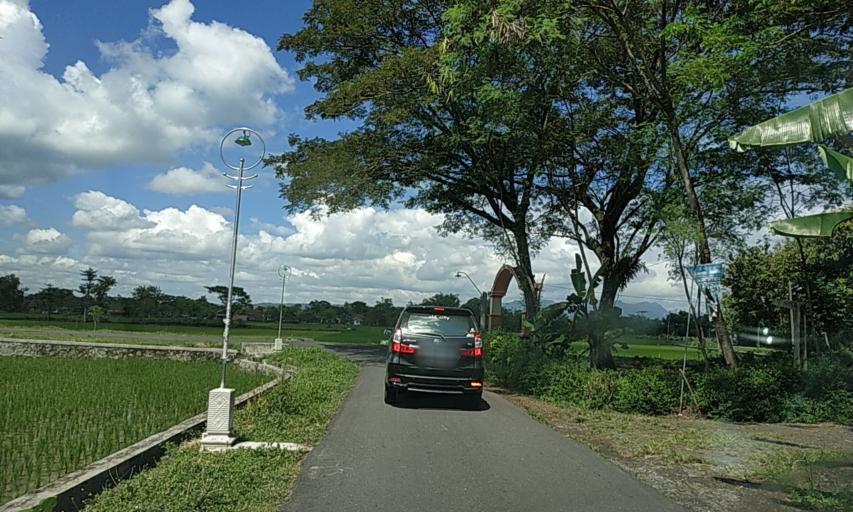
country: ID
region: Central Java
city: Trucuk
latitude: -7.7401
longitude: 110.7233
